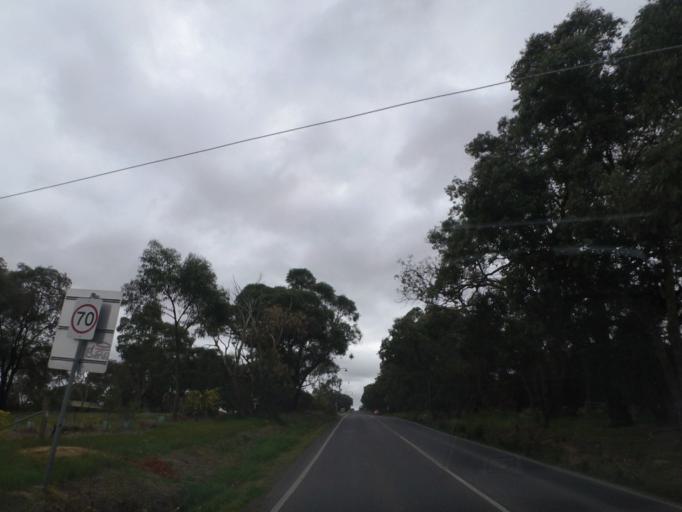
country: AU
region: Victoria
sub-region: Nillumbik
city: Doreen
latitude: -37.6212
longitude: 145.1355
